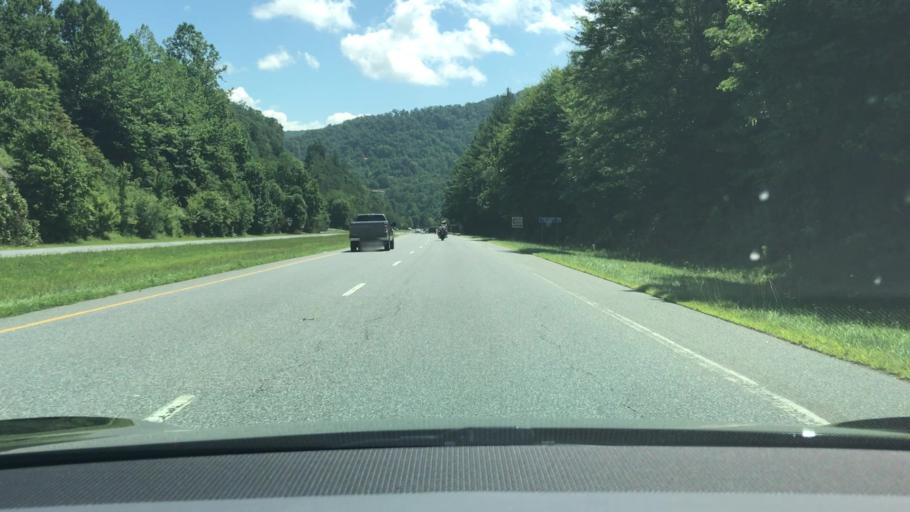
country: US
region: North Carolina
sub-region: Jackson County
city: Sylva
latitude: 35.2924
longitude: -83.2759
